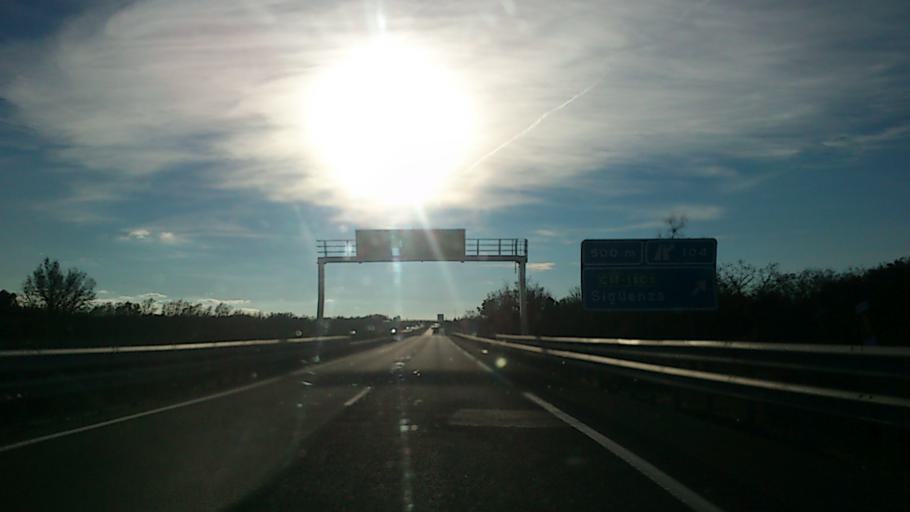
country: ES
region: Castille-La Mancha
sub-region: Provincia de Guadalajara
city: Mirabueno
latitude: 40.9188
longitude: -2.7296
